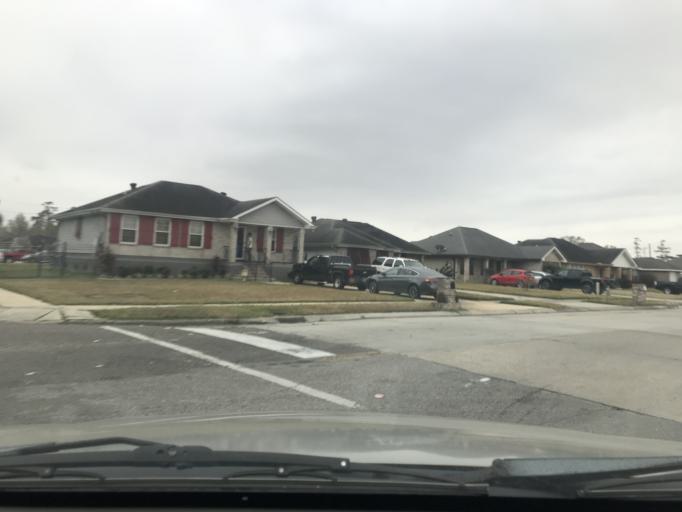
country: US
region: Louisiana
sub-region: Jefferson Parish
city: Woodmere
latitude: 29.8582
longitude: -90.0716
